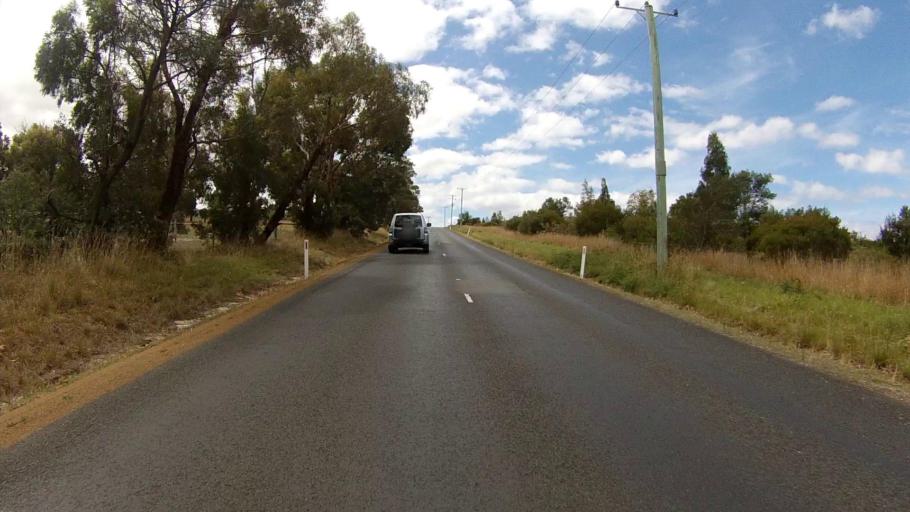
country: AU
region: Tasmania
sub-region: Sorell
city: Sorell
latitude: -42.8163
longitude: 147.6128
